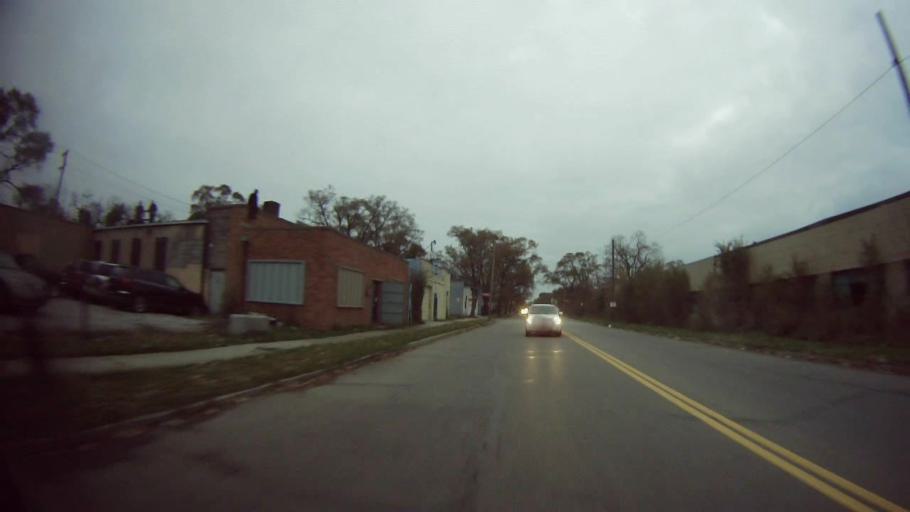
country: US
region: Michigan
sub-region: Wayne County
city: Hamtramck
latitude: 42.4268
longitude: -83.0628
